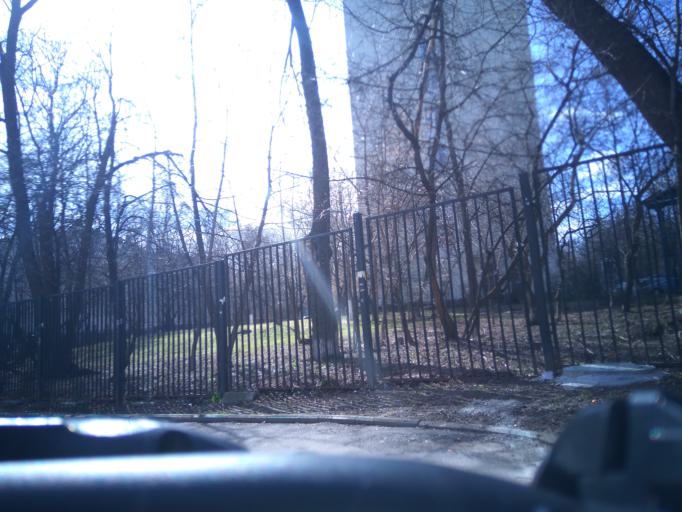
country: RU
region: Moskovskaya
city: Fili
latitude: 55.7422
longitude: 37.4867
